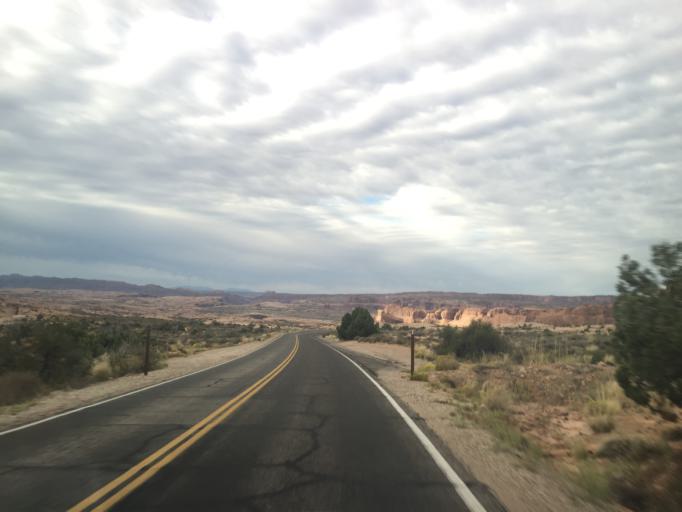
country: US
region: Utah
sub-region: Grand County
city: Moab
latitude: 38.6851
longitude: -109.5820
